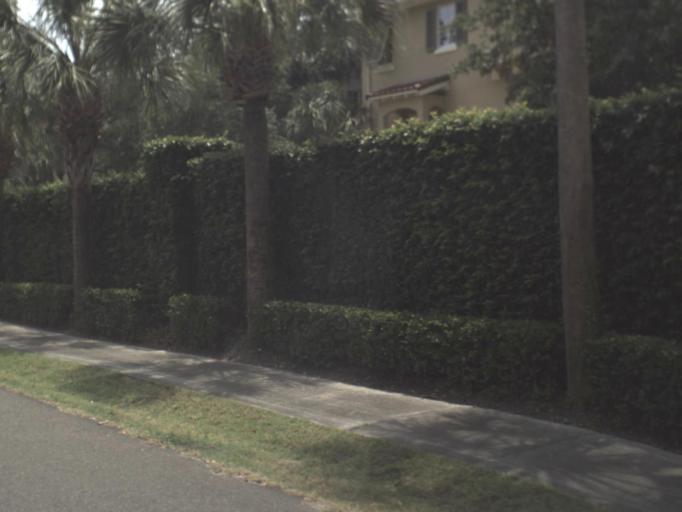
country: US
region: Florida
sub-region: Nassau County
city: Fernandina Beach
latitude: 30.5821
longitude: -81.4546
